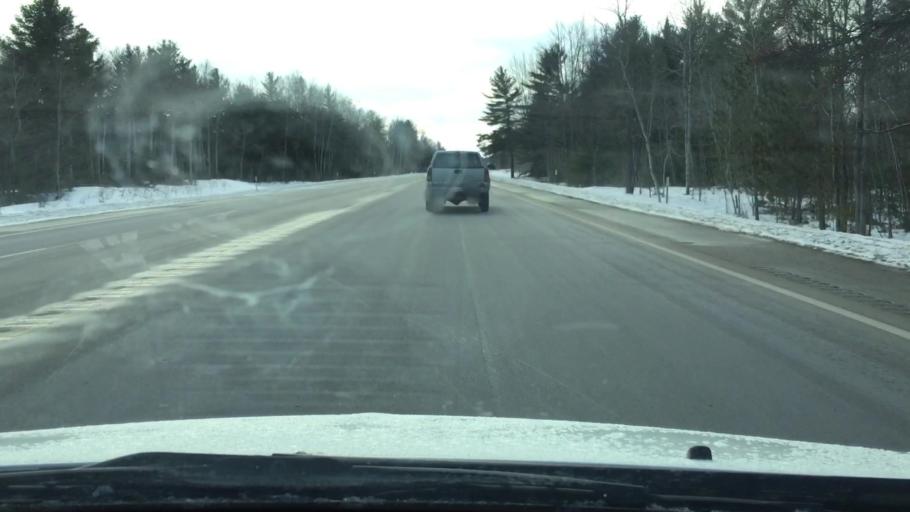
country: US
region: Michigan
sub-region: Kalkaska County
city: Kalkaska
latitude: 44.6658
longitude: -85.2461
